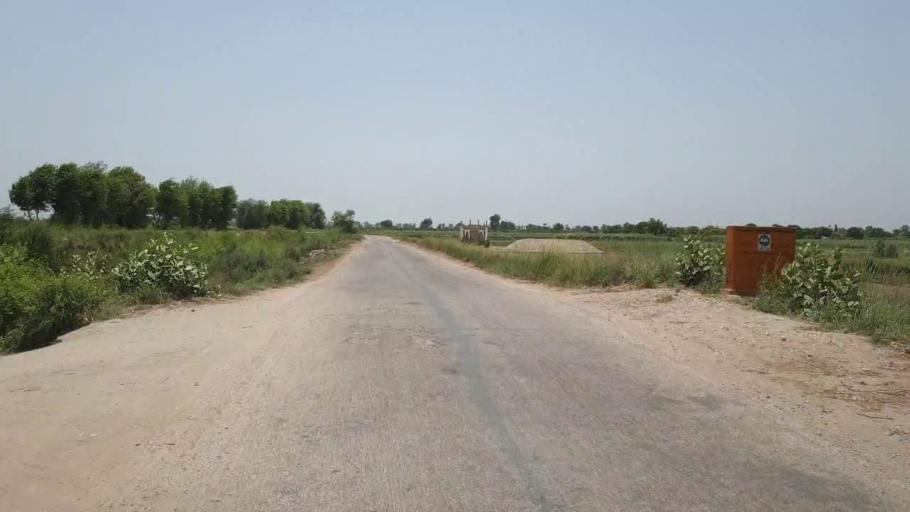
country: PK
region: Sindh
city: Daur
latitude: 26.3854
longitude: 68.1824
